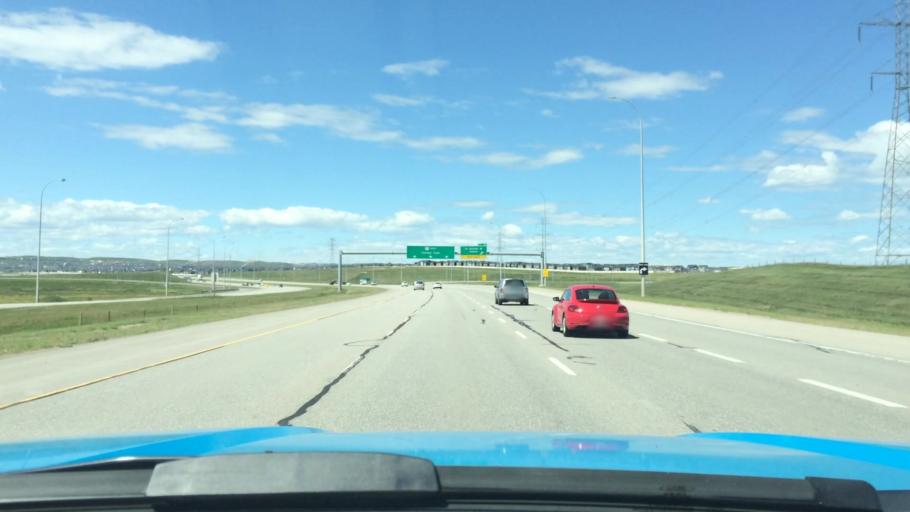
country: CA
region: Alberta
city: Calgary
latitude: 51.1746
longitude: -114.0824
